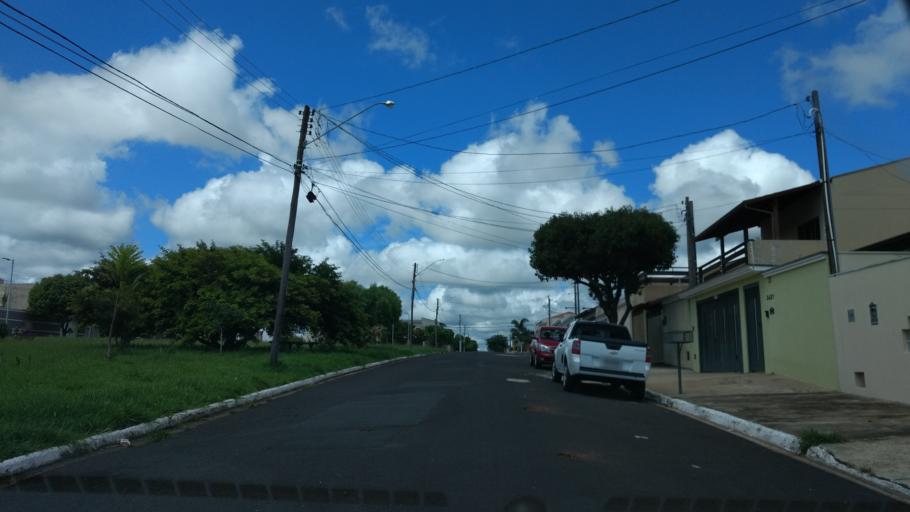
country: BR
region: Sao Paulo
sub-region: Botucatu
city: Botucatu
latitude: -22.8571
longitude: -48.4474
